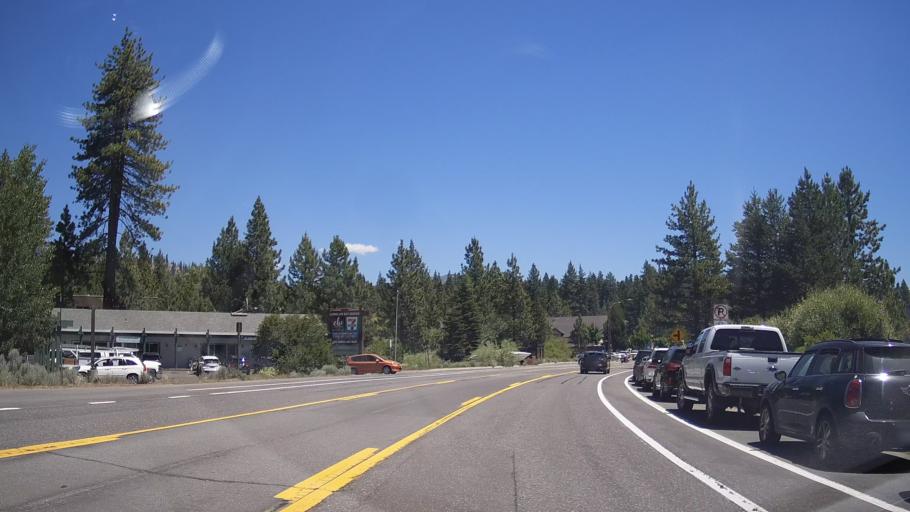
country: US
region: California
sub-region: Placer County
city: Tahoe Vista
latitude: 39.2264
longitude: -120.0825
